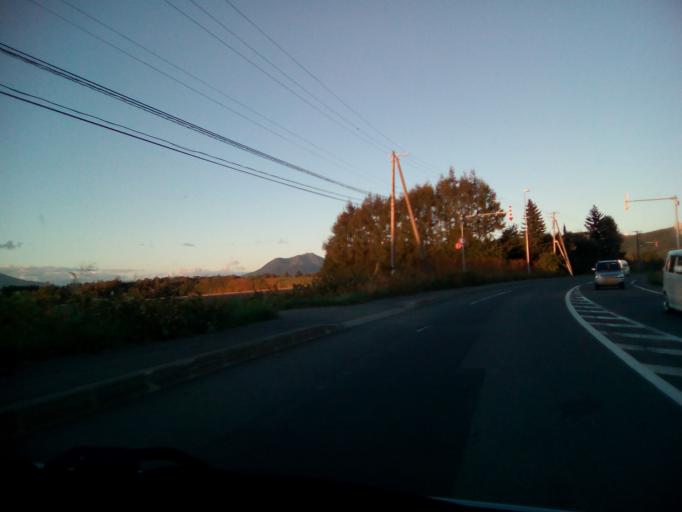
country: JP
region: Hokkaido
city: Niseko Town
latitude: 42.6637
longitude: 140.8130
